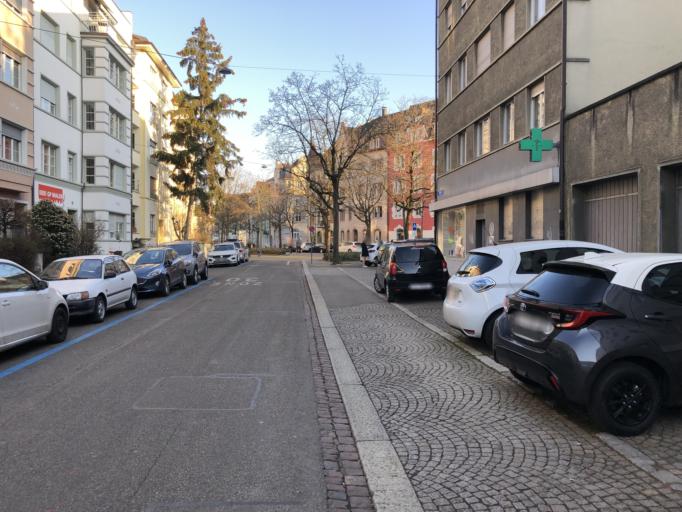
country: CH
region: Basel-City
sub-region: Basel-Stadt
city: Basel
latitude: 47.5579
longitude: 7.5724
